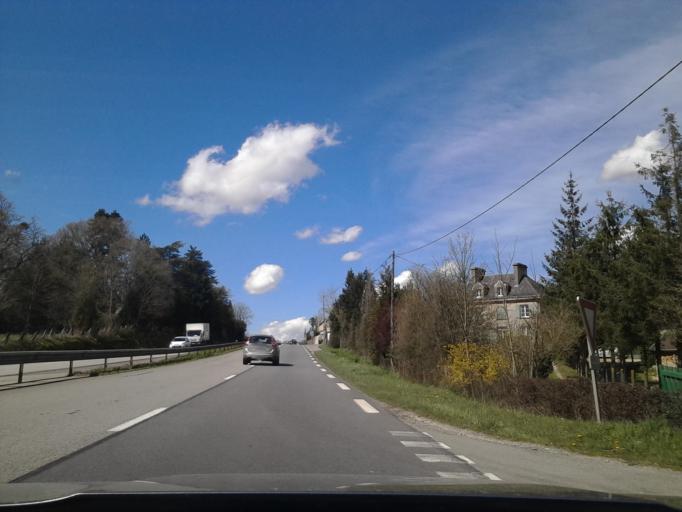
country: FR
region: Lower Normandy
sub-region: Departement de la Manche
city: Valognes
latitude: 49.5252
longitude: -1.5089
